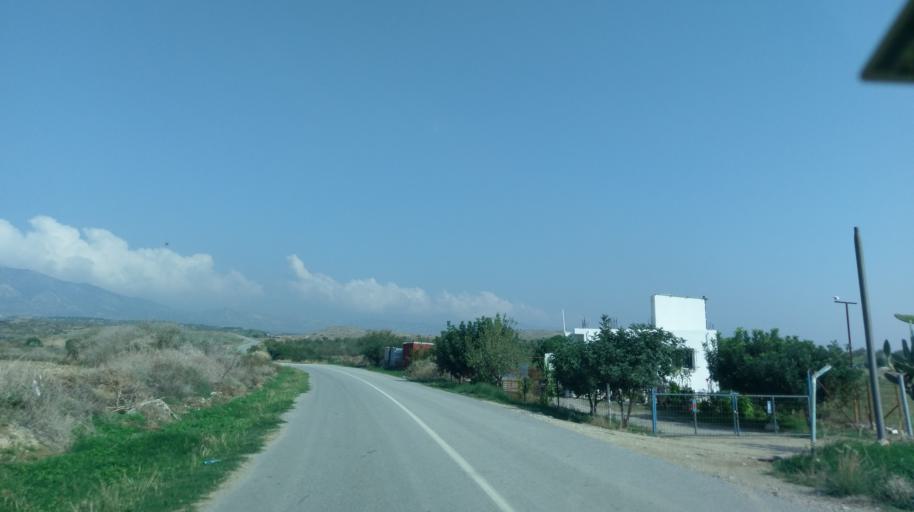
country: CY
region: Ammochostos
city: Lefkonoiko
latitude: 35.2616
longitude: 33.6093
